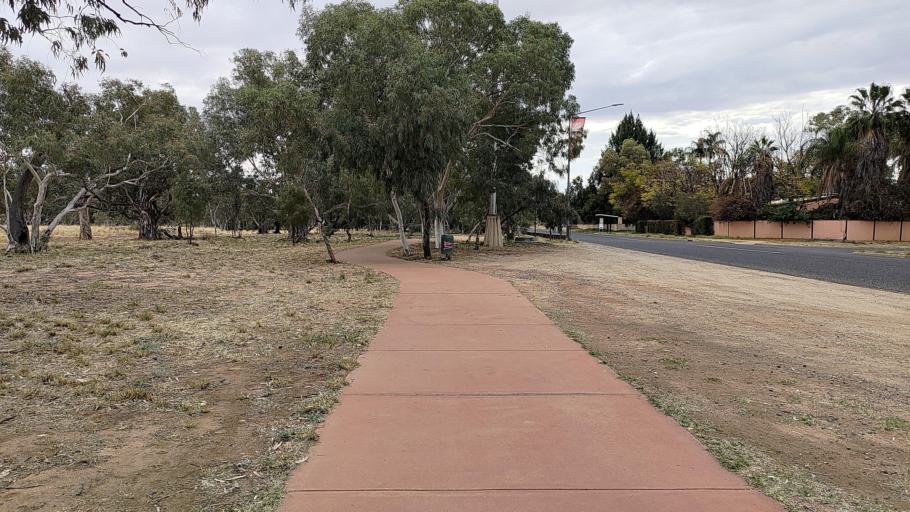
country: AU
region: Northern Territory
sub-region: Alice Springs
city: Alice Springs
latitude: -23.7099
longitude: 133.8808
